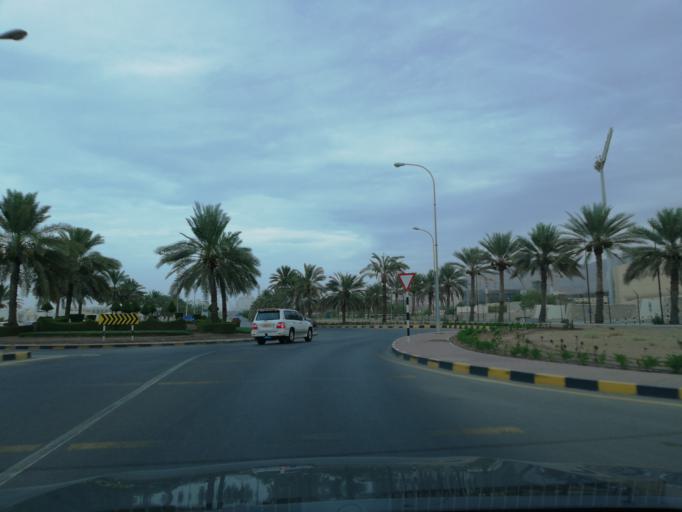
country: OM
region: Muhafazat Masqat
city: Bawshar
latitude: 23.5746
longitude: 58.3983
